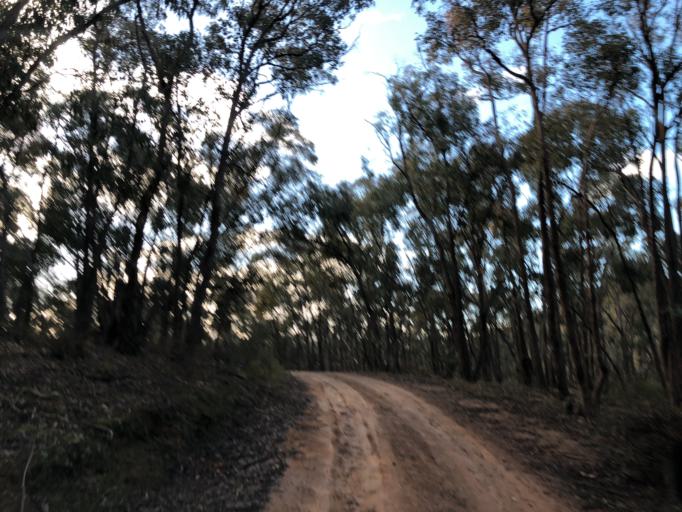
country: AU
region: Victoria
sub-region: Mount Alexander
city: Castlemaine
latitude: -37.2238
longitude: 144.2647
